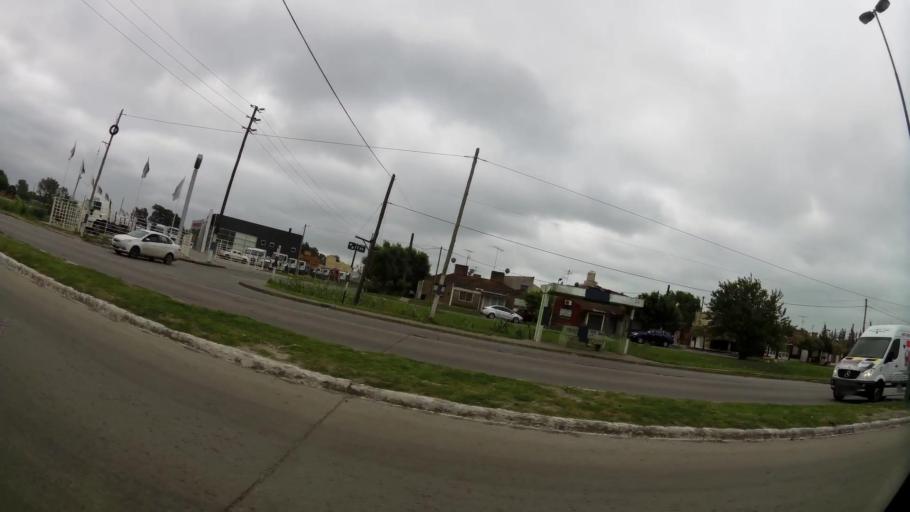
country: AR
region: Buenos Aires
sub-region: Partido de La Plata
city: La Plata
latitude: -34.9887
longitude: -58.0408
